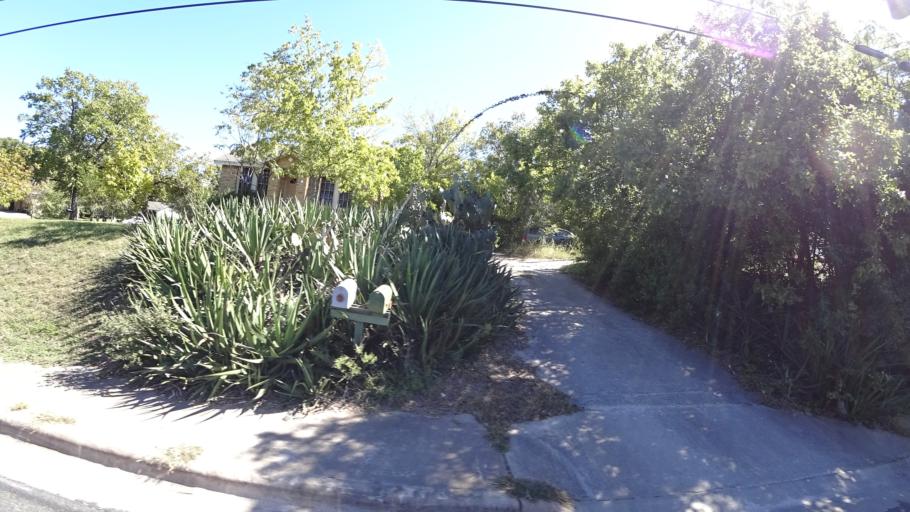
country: US
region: Texas
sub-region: Travis County
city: Austin
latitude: 30.2317
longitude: -97.7694
